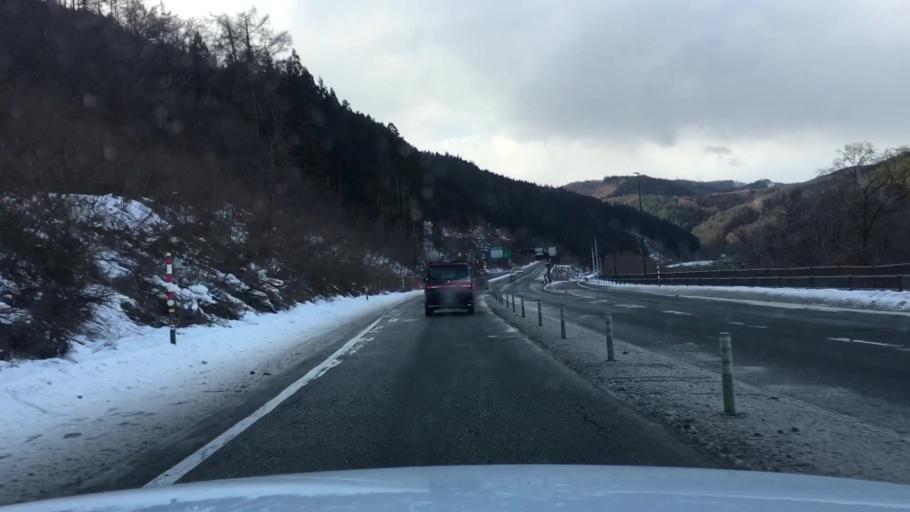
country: JP
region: Iwate
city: Morioka-shi
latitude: 39.6687
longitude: 141.2349
